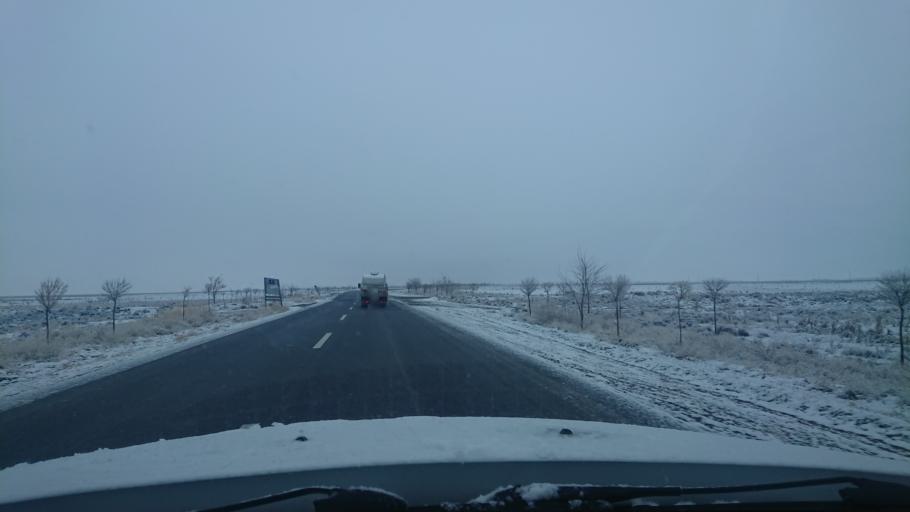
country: TR
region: Aksaray
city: Yesilova
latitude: 38.3091
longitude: 33.7543
